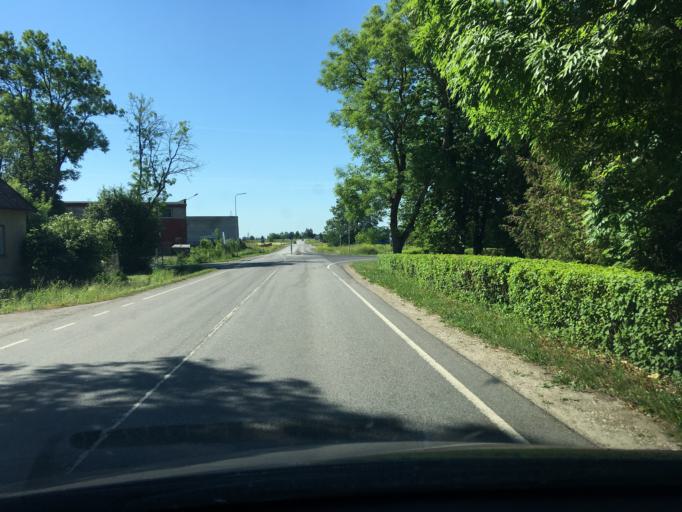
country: EE
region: Harju
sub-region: Raasiku vald
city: Raasiku
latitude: 59.3769
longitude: 25.1942
